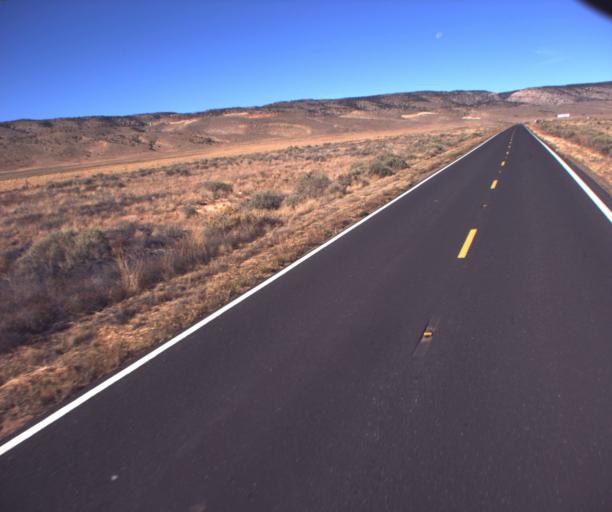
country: US
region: Arizona
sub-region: Coconino County
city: Fredonia
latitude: 36.7272
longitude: -112.0328
